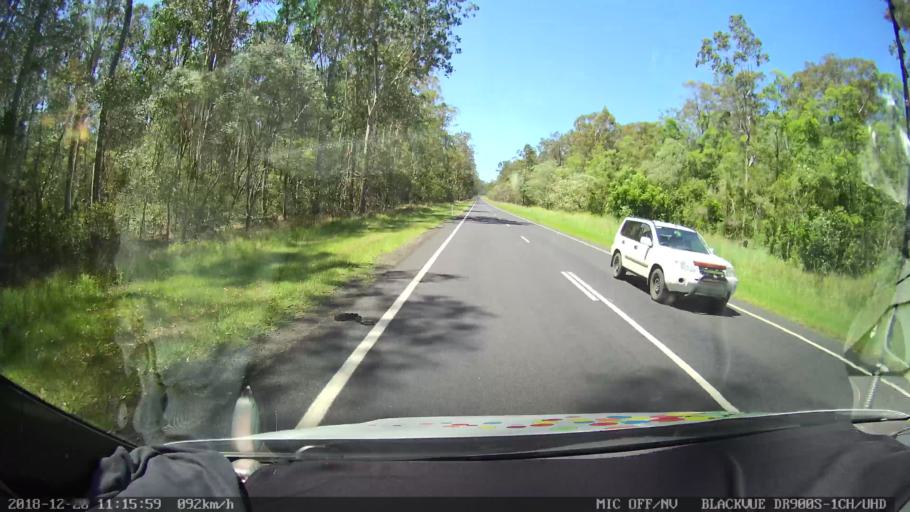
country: AU
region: New South Wales
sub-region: Richmond Valley
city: Casino
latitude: -29.0204
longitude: 153.0112
